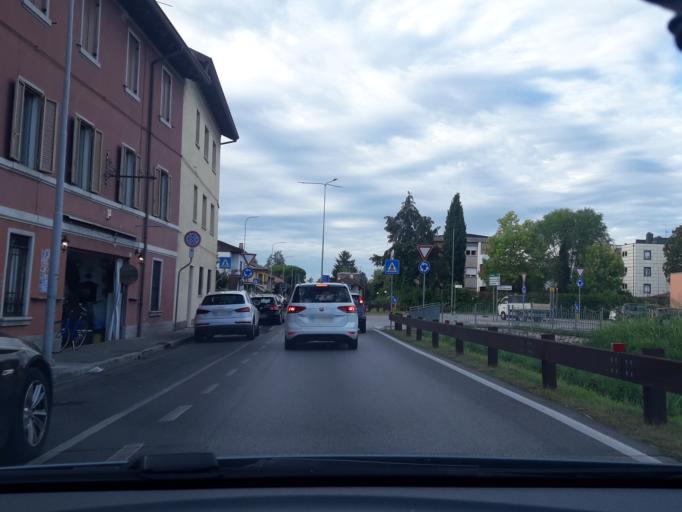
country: IT
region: Friuli Venezia Giulia
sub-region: Provincia di Udine
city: Basaldella
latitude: 46.0487
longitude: 13.2236
